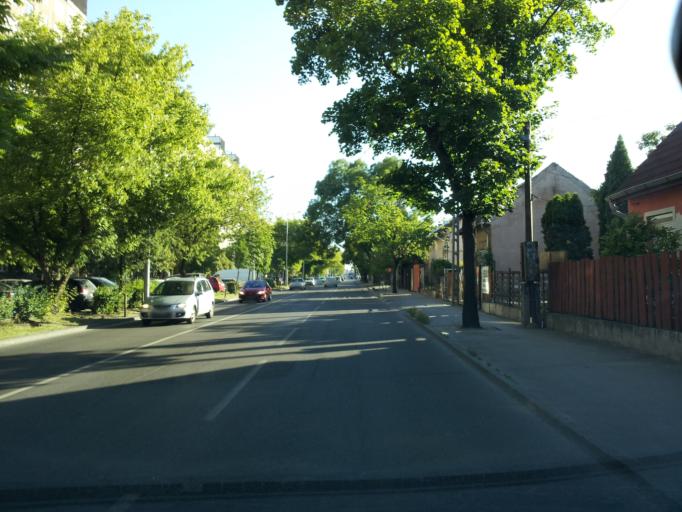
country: HU
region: Budapest
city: Budapest XIV. keruelet
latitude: 47.5353
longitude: 19.1326
